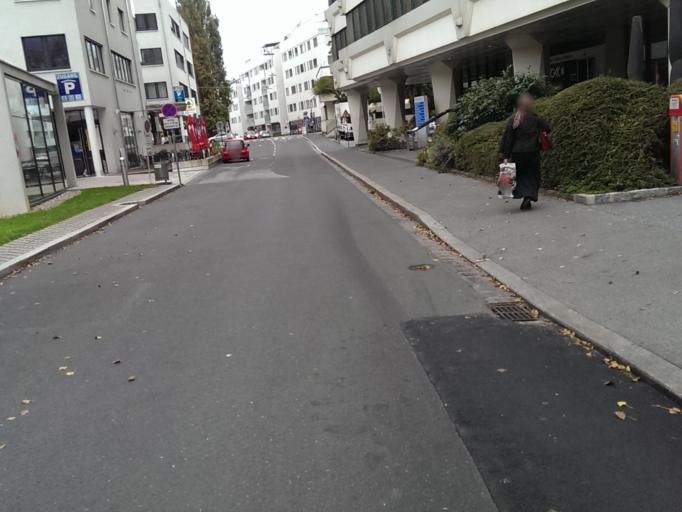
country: AT
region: Styria
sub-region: Graz Stadt
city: Graz
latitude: 47.0651
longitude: 15.4366
